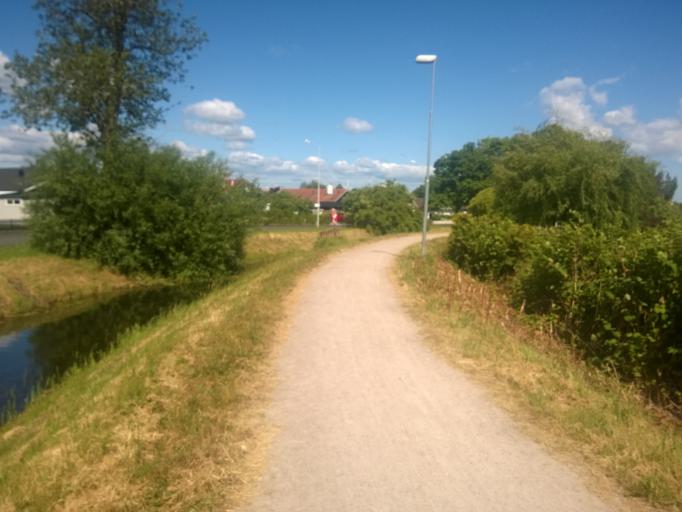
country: SE
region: Skane
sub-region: Kristianstads Kommun
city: Kristianstad
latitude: 56.0493
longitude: 14.1712
